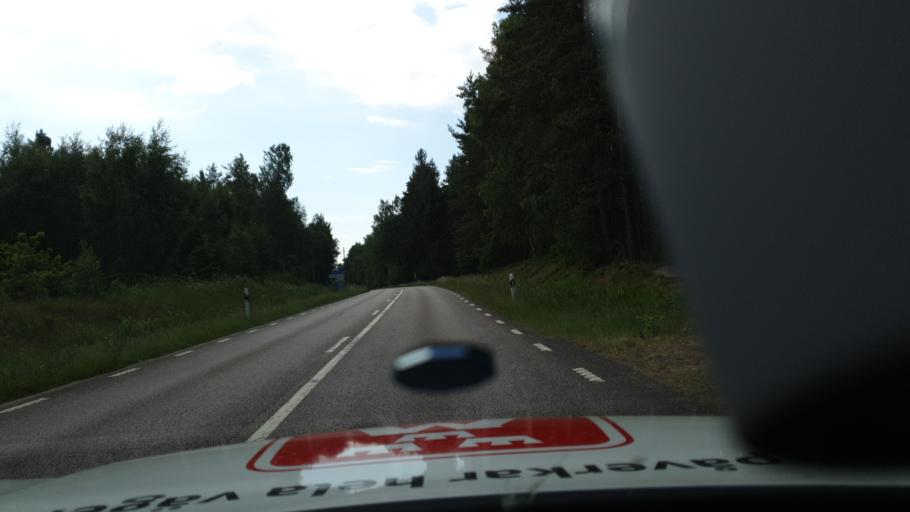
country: SE
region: Vaestra Goetaland
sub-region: Hjo Kommun
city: Hjo
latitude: 58.1846
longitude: 14.2026
